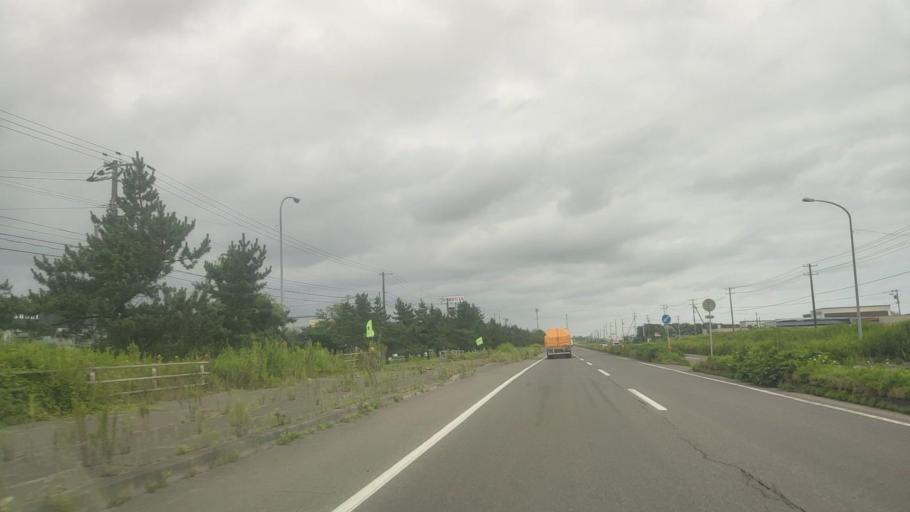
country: JP
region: Hokkaido
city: Shiraoi
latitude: 42.5323
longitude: 141.3255
